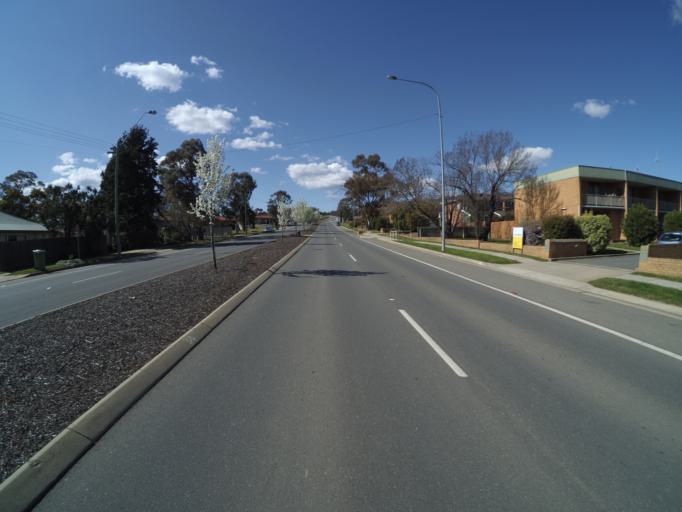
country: AU
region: New South Wales
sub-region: Queanbeyan
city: Queanbeyan
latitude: -35.3468
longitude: 149.2471
